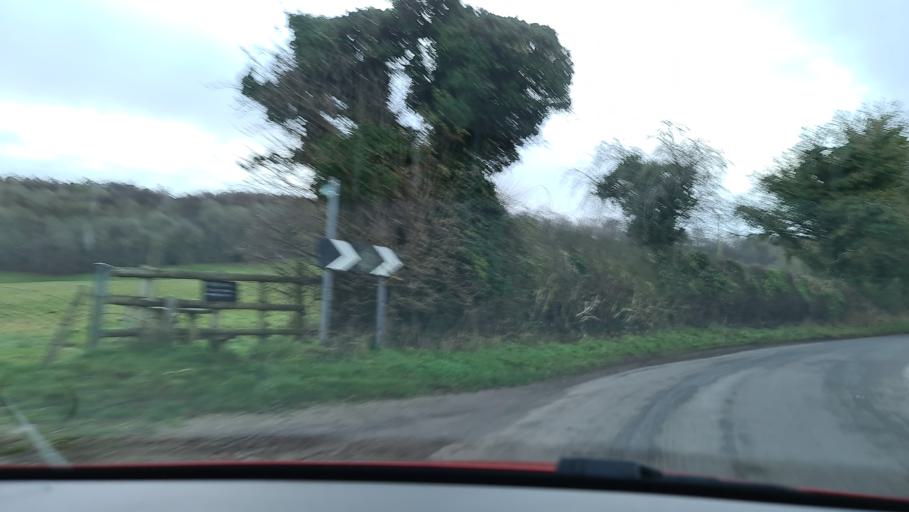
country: GB
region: England
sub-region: Buckinghamshire
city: Princes Risborough
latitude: 51.7139
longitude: -0.8123
